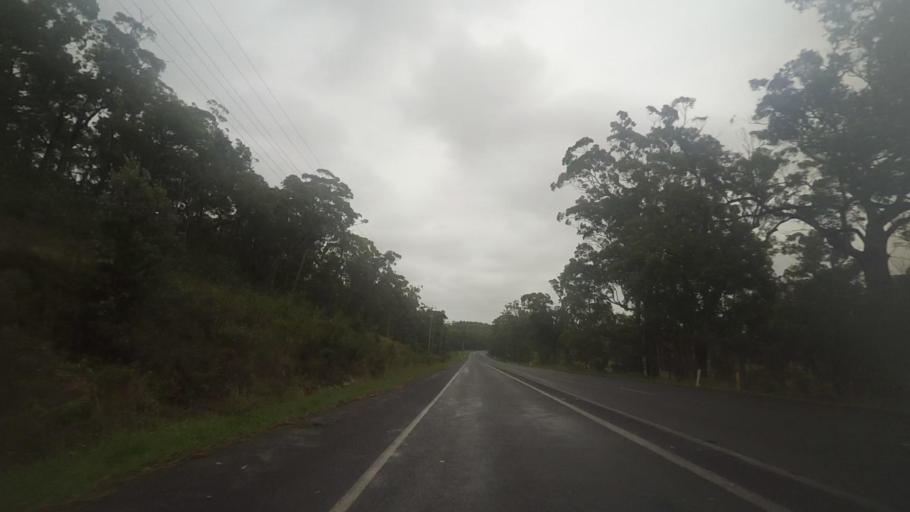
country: AU
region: New South Wales
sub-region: Port Stephens Shire
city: Port Stephens
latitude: -32.6452
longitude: 151.9827
